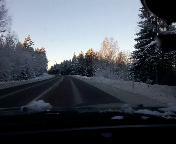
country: SE
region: Gaevleborg
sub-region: Ljusdals Kommun
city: Ljusdal
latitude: 61.7931
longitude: 16.1288
